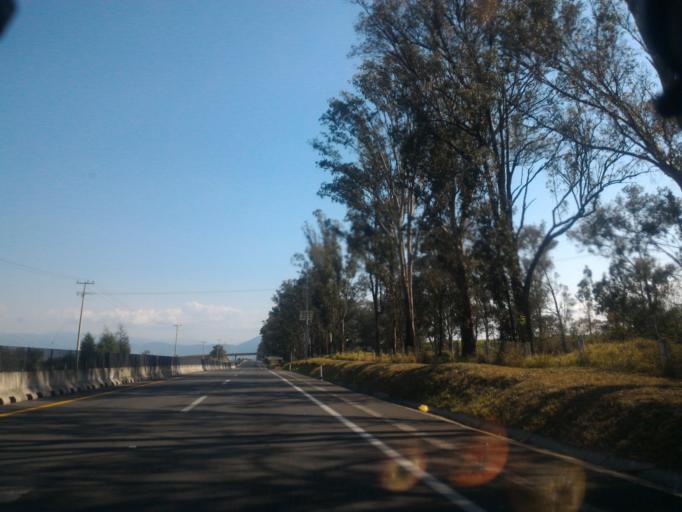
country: MX
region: Jalisco
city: Zapotiltic
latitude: 19.6003
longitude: -103.4549
